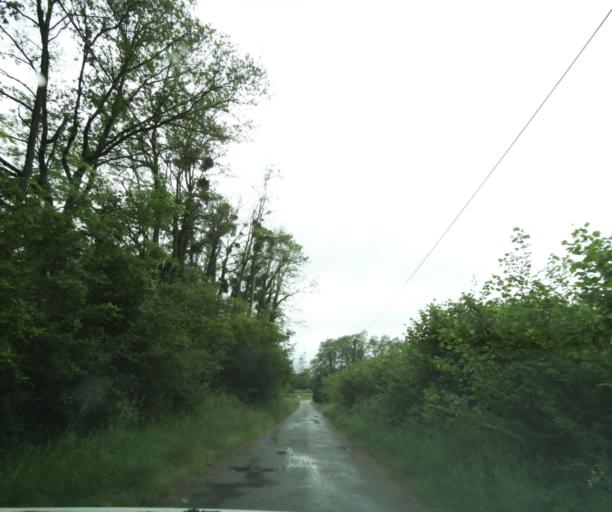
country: FR
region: Bourgogne
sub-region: Departement de Saone-et-Loire
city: Ciry-le-Noble
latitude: 46.5237
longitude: 4.3029
